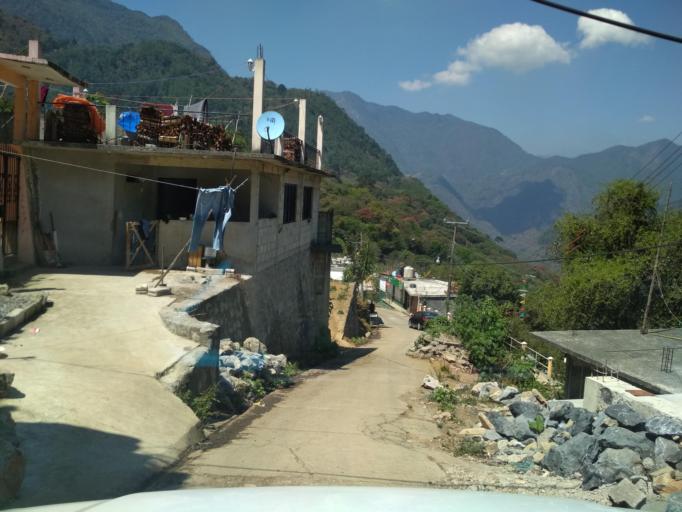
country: MX
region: Veracruz
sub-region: Tlilapan
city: Tonalixco
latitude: 18.7766
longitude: -97.0764
